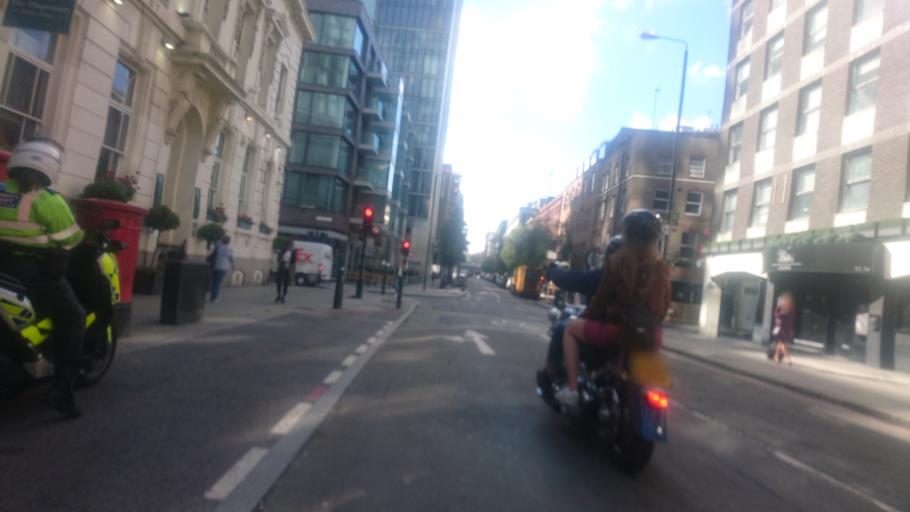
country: GB
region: England
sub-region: Greater London
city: Bethnal Green
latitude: 51.5142
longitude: -0.0707
